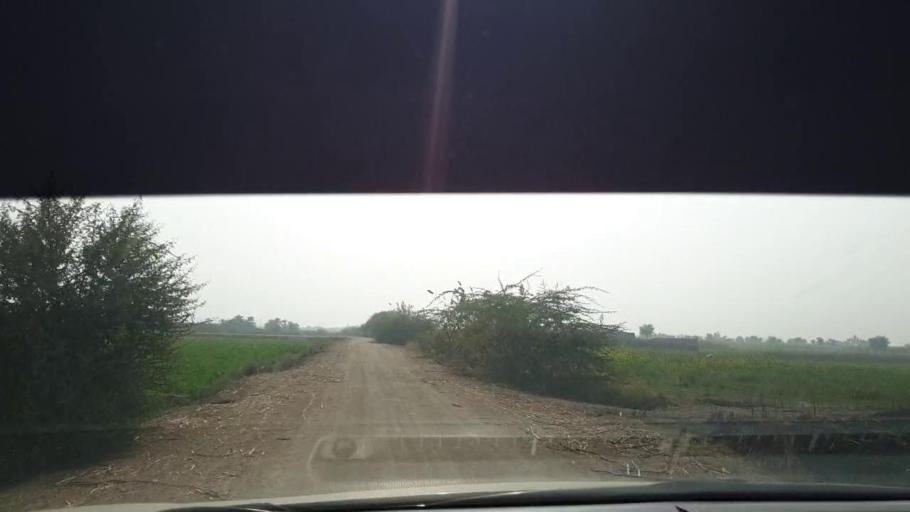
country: PK
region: Sindh
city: Berani
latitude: 25.8299
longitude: 68.8403
